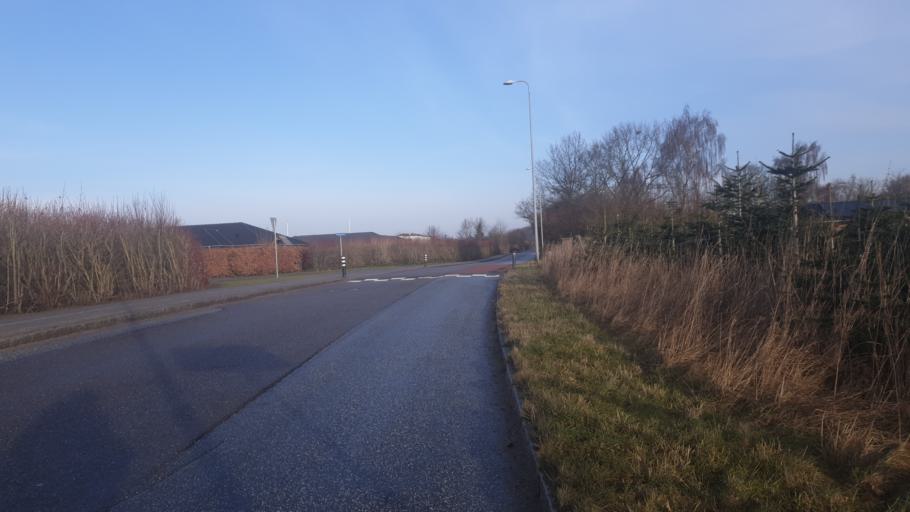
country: DK
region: Central Jutland
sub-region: Hedensted Kommune
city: Hedensted
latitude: 55.7668
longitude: 9.7214
